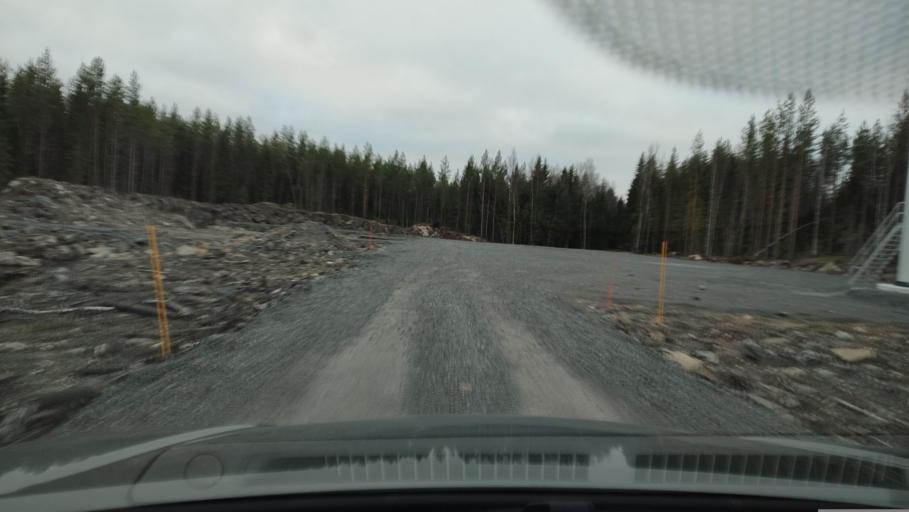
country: FI
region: Southern Ostrobothnia
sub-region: Suupohja
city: Karijoki
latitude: 62.1806
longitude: 21.5708
